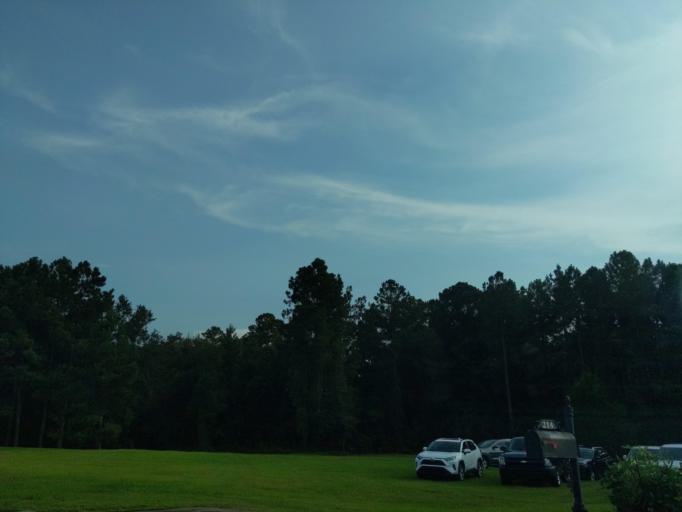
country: US
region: Georgia
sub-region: Thomas County
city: Thomasville
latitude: 30.8957
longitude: -83.9389
